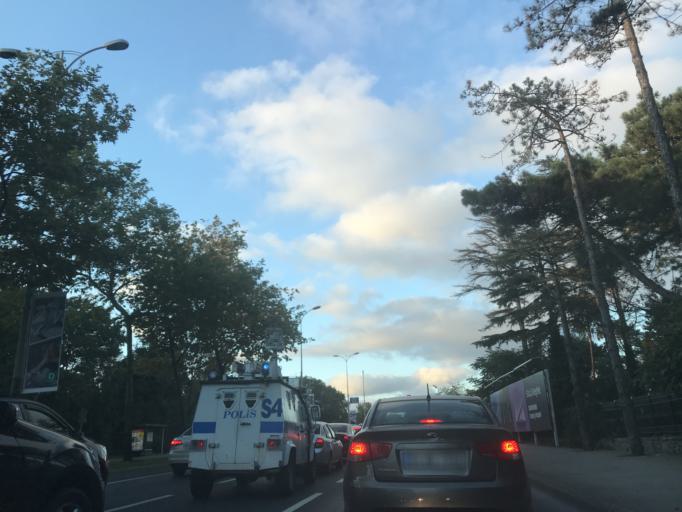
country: TR
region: Istanbul
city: Sisli
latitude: 41.1339
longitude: 29.0251
